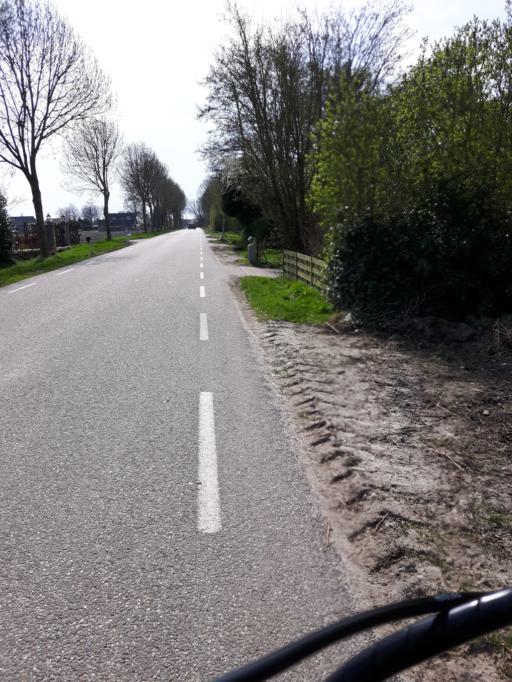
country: NL
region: Zeeland
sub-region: Gemeente Goes
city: Goes
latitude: 51.5058
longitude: 3.9492
